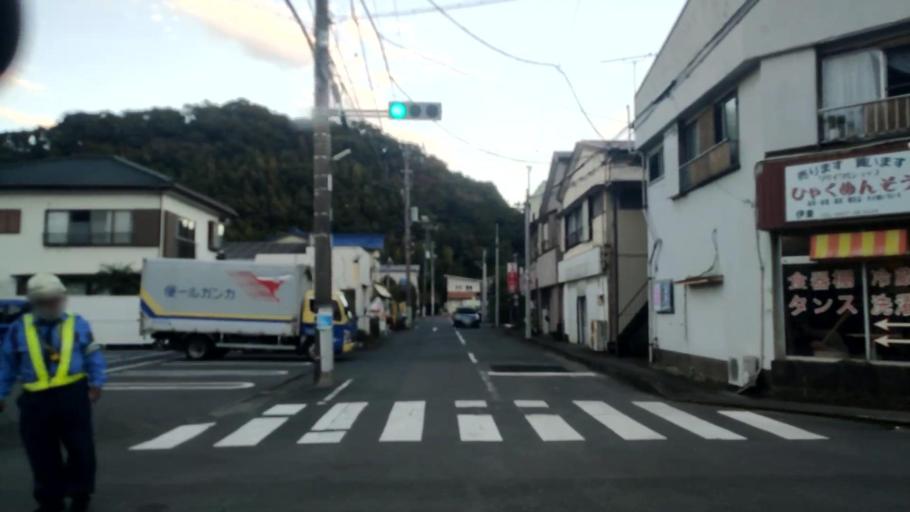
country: JP
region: Shizuoka
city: Ito
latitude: 34.9580
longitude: 139.0895
